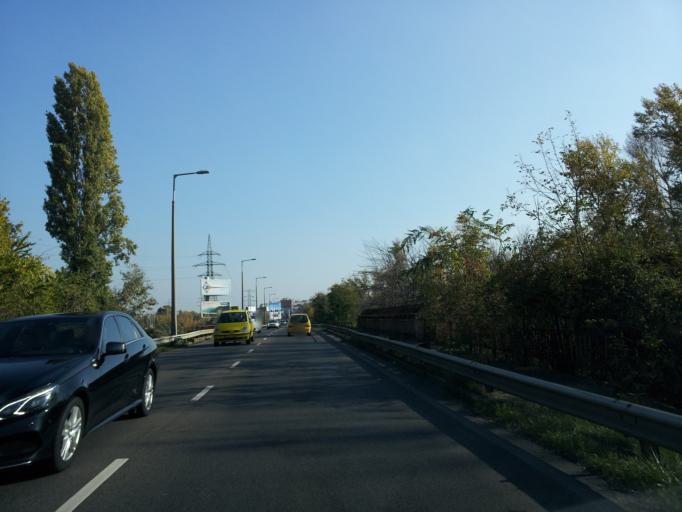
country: HU
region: Budapest
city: Budapest XIX. keruelet
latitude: 47.4655
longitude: 19.1355
